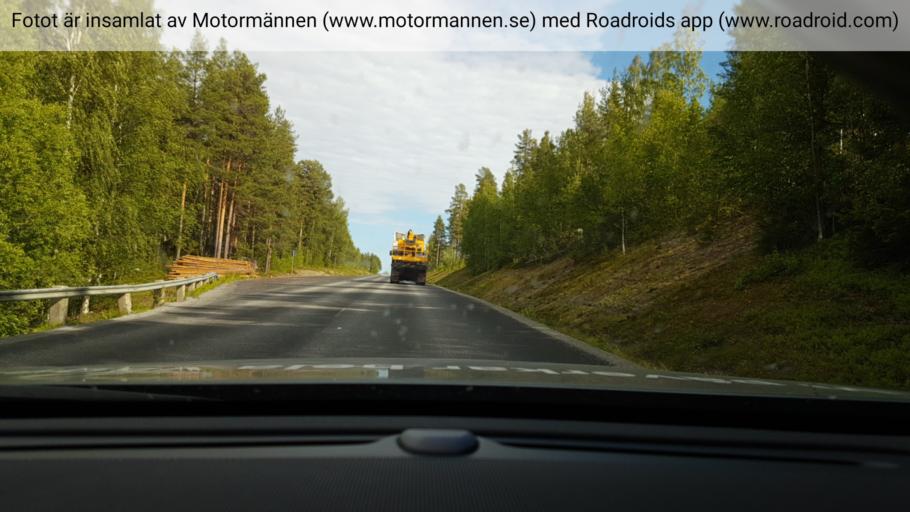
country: SE
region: Vaesterbotten
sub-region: Lycksele Kommun
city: Soderfors
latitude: 64.8410
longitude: 17.9778
